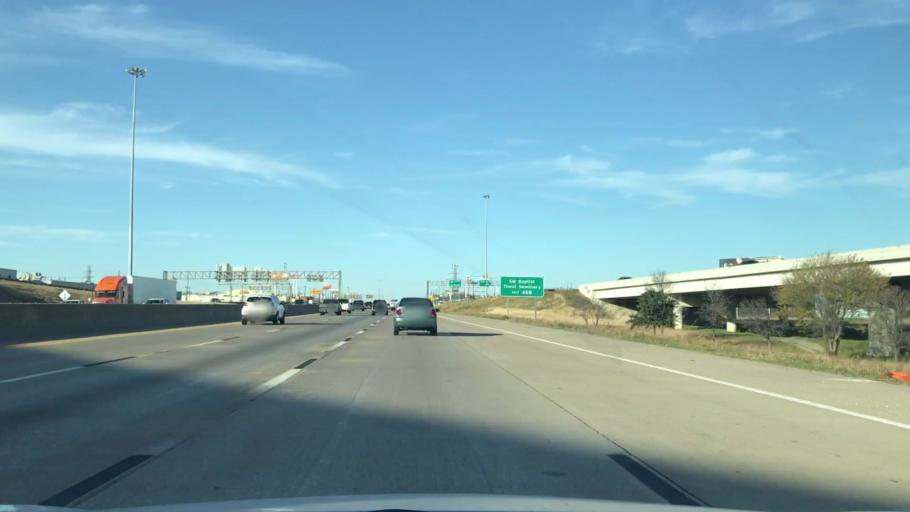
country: US
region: Texas
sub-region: Tarrant County
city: Edgecliff Village
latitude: 32.6691
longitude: -97.3202
